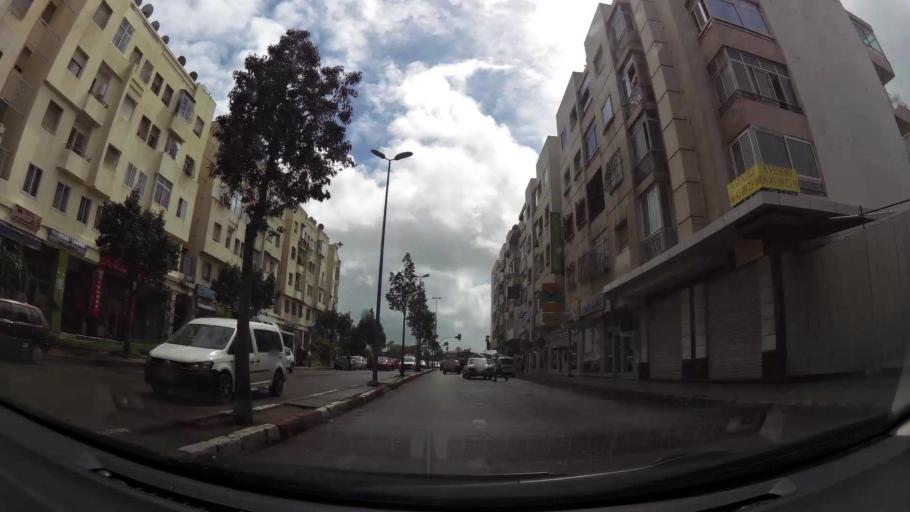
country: MA
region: Grand Casablanca
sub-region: Casablanca
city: Casablanca
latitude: 33.5260
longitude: -7.6505
